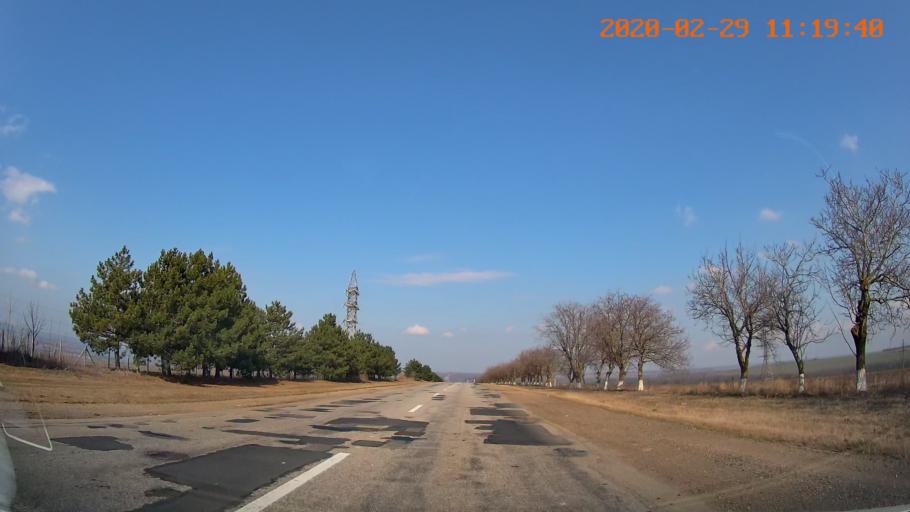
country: MD
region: Telenesti
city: Cocieri
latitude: 47.3536
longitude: 29.1739
